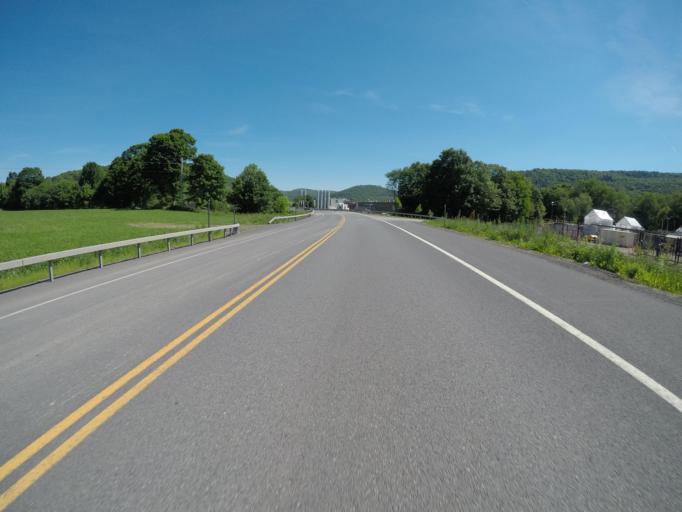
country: US
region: New York
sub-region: Delaware County
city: Delhi
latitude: 42.2424
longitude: -74.9653
